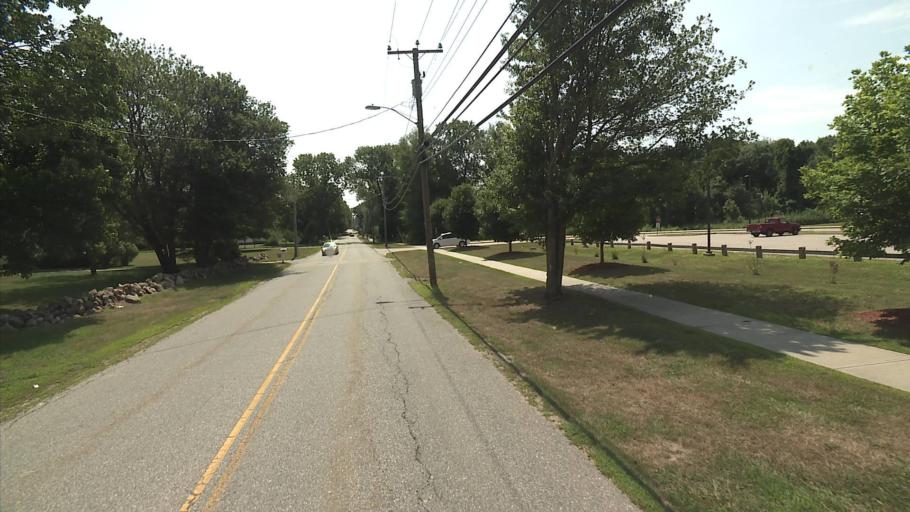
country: US
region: Connecticut
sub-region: New London County
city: Central Waterford
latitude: 41.3137
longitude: -72.1324
